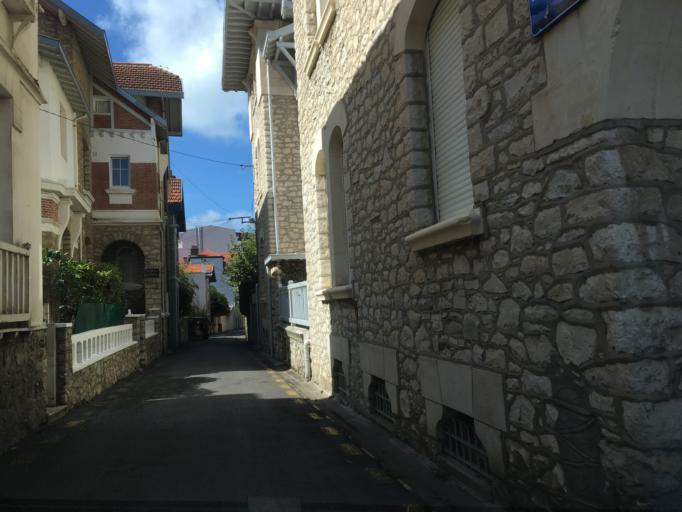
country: FR
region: Aquitaine
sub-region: Departement des Pyrenees-Atlantiques
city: Biarritz
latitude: 43.4844
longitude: -1.5489
